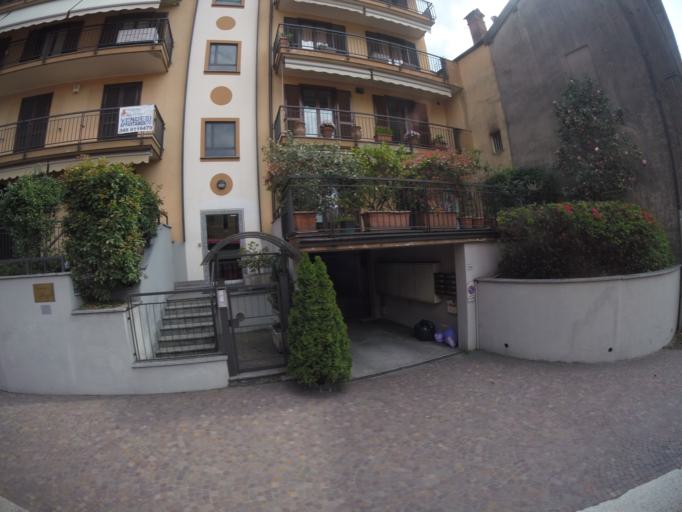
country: IT
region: Piedmont
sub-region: Provincia Verbano-Cusio-Ossola
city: Omegna
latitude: 45.8748
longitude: 8.4115
